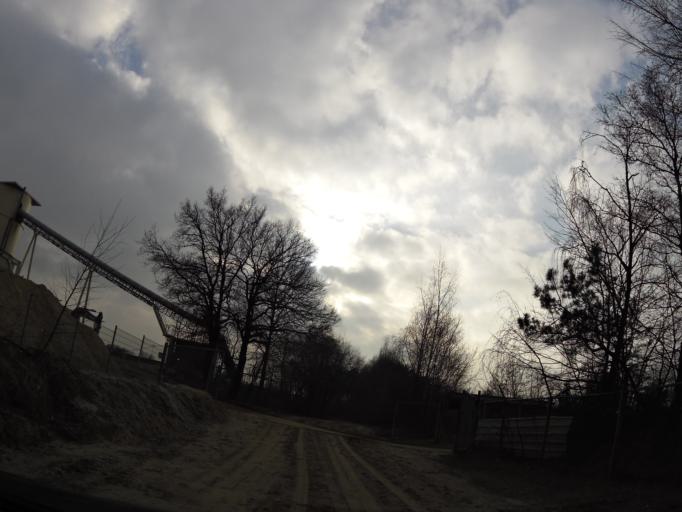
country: NL
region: Limburg
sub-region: Gemeente Brunssum
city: Brunssum
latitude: 50.9249
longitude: 6.0275
